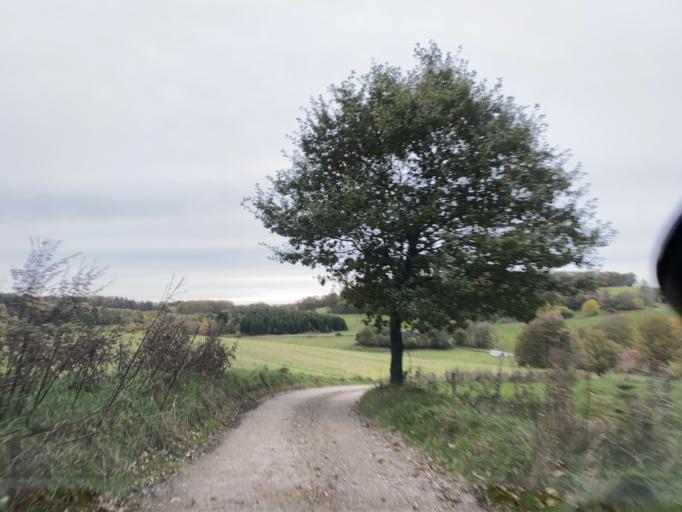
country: DK
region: Central Jutland
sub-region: Favrskov Kommune
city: Hammel
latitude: 56.1941
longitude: 9.7819
